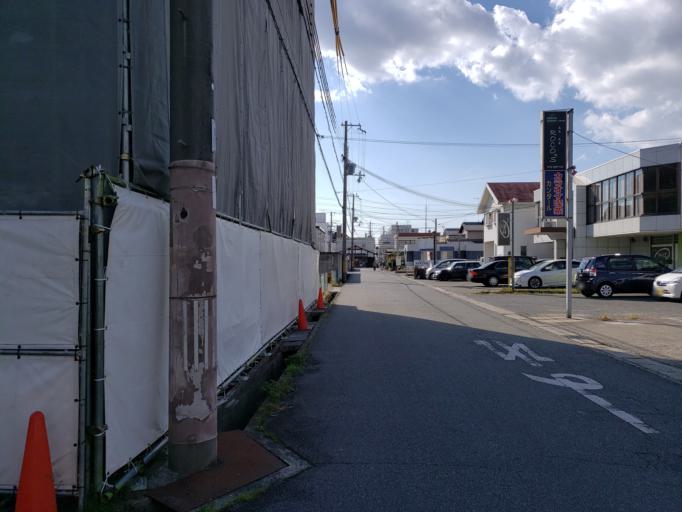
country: JP
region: Hyogo
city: Kakogawacho-honmachi
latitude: 34.7583
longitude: 134.8395
